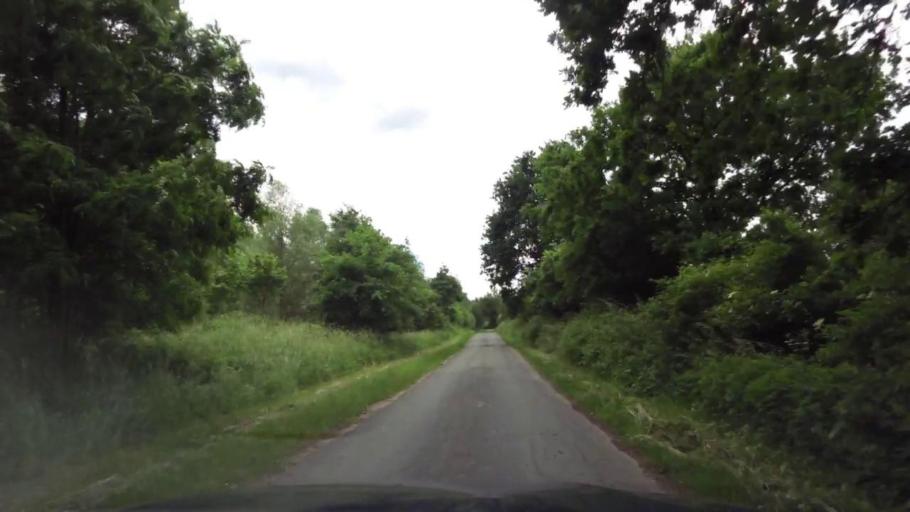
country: PL
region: West Pomeranian Voivodeship
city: Trzcinsko Zdroj
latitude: 52.8777
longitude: 14.5843
